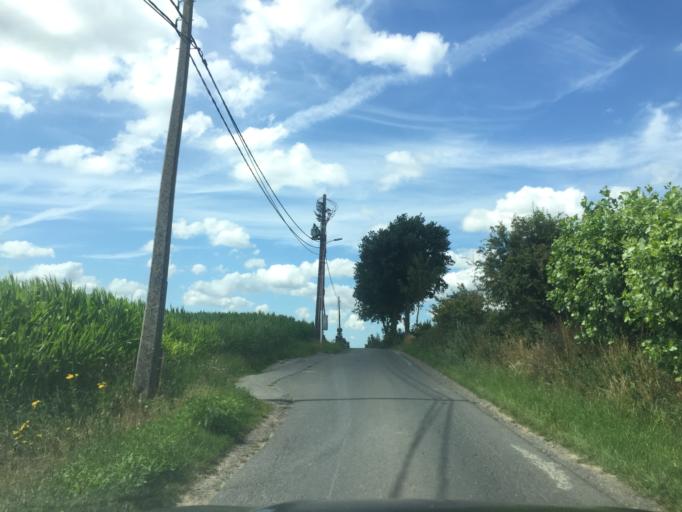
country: BE
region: Flanders
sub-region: Provincie West-Vlaanderen
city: Staden
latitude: 50.9503
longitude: 3.0082
